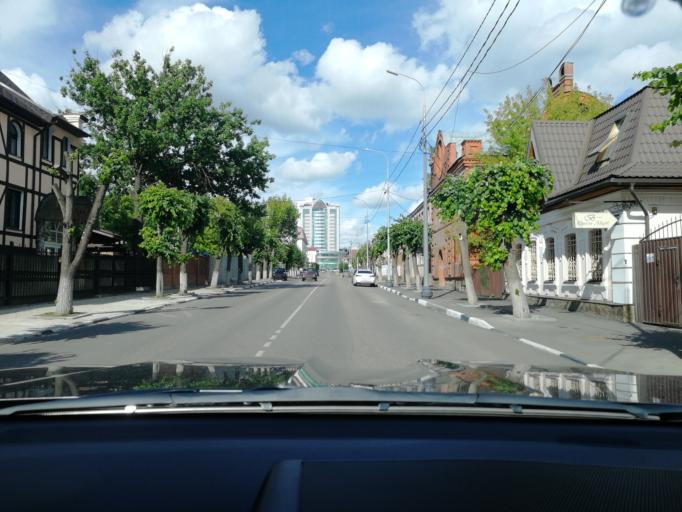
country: RU
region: Moskovskaya
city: Serpukhov
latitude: 54.9147
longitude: 37.4198
